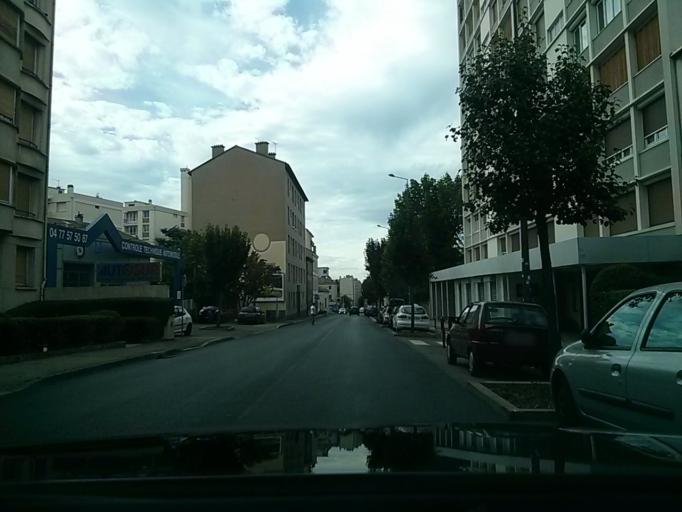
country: FR
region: Rhone-Alpes
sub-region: Departement de la Loire
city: Saint-Etienne
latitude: 45.4122
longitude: 4.3973
